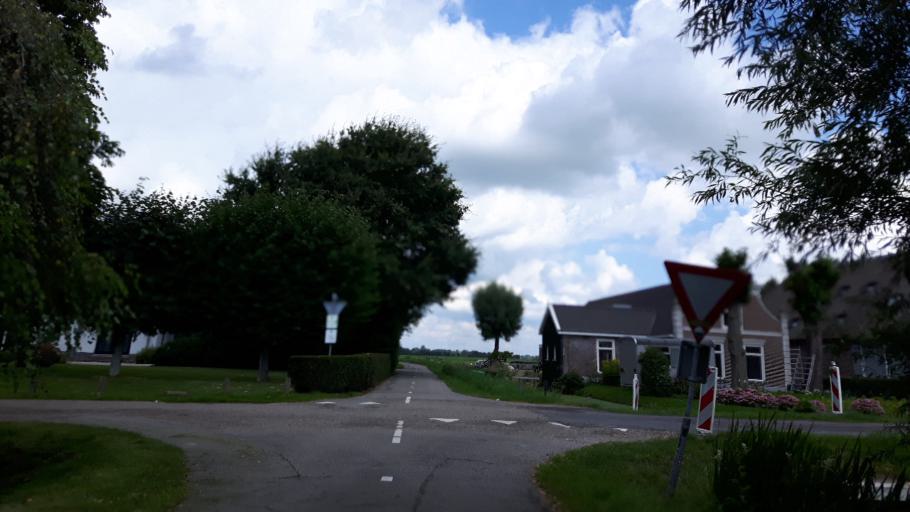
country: NL
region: Utrecht
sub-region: Gemeente Woerden
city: Woerden
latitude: 52.1059
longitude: 4.9224
